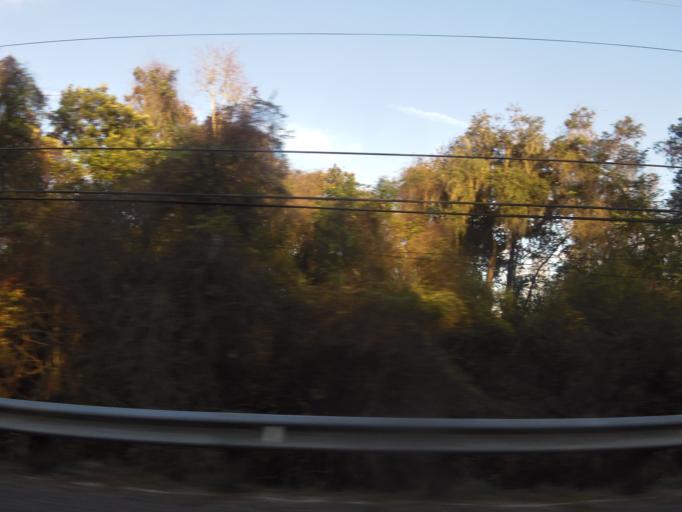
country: US
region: Florida
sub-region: Putnam County
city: East Palatka
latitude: 29.8362
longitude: -81.5537
